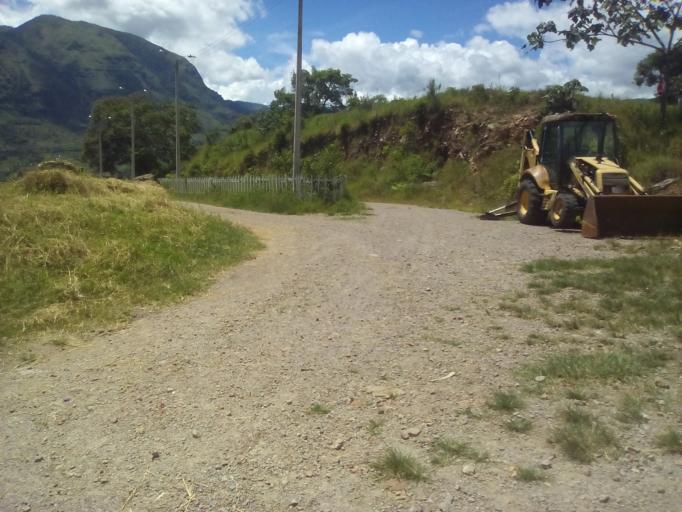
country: CO
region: Casanare
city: Nunchia
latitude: 5.6256
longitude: -72.4247
